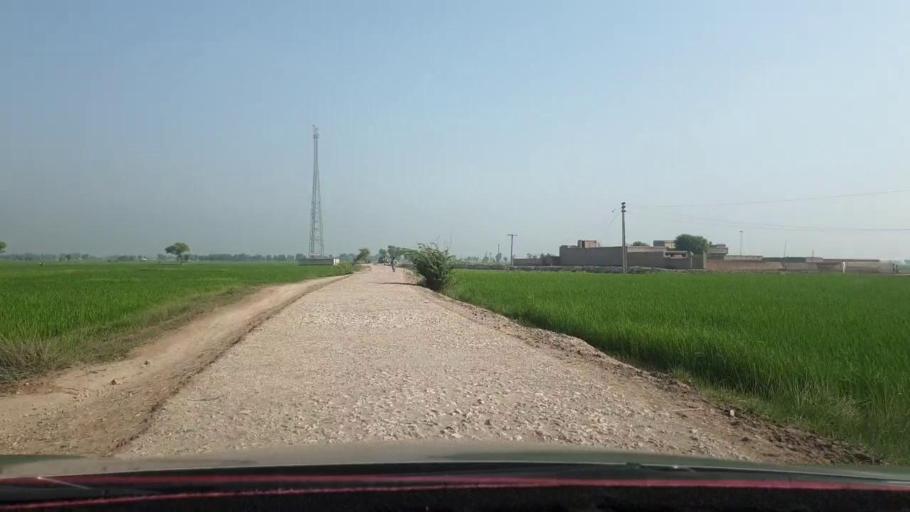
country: PK
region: Sindh
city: Nasirabad
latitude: 27.4843
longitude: 67.9256
